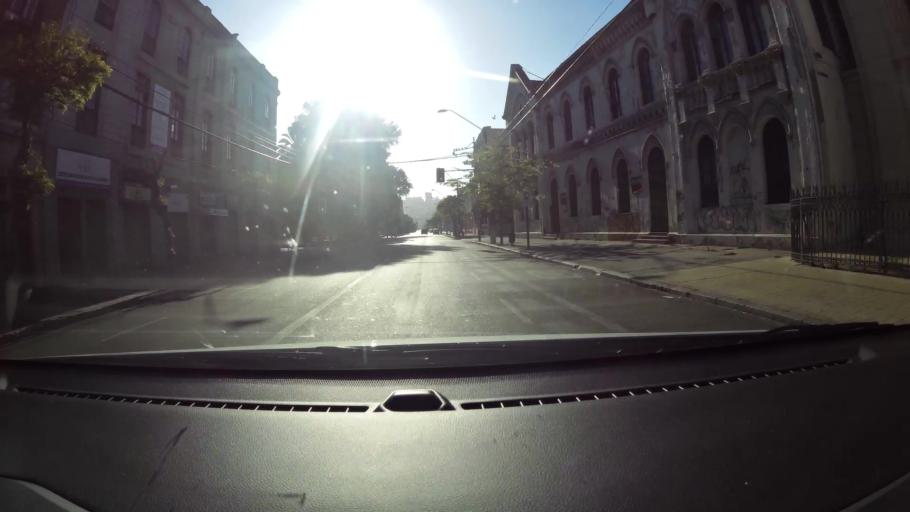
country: CL
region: Valparaiso
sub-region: Provincia de Valparaiso
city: Valparaiso
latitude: -33.0482
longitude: -71.6152
